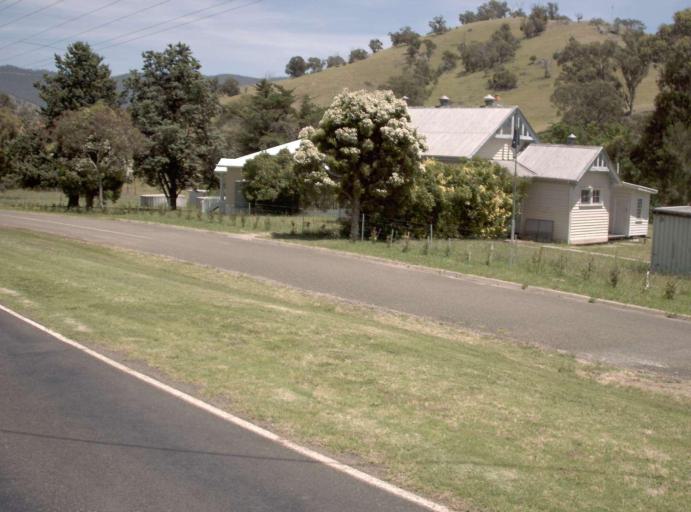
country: AU
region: Victoria
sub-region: East Gippsland
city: Bairnsdale
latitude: -37.3760
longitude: 147.8348
